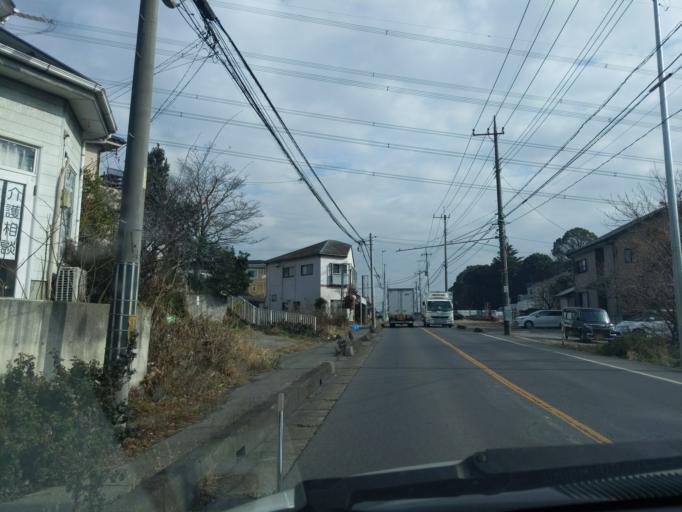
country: JP
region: Saitama
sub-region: Kawaguchi-shi
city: Hatogaya-honcho
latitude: 35.8606
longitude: 139.7408
